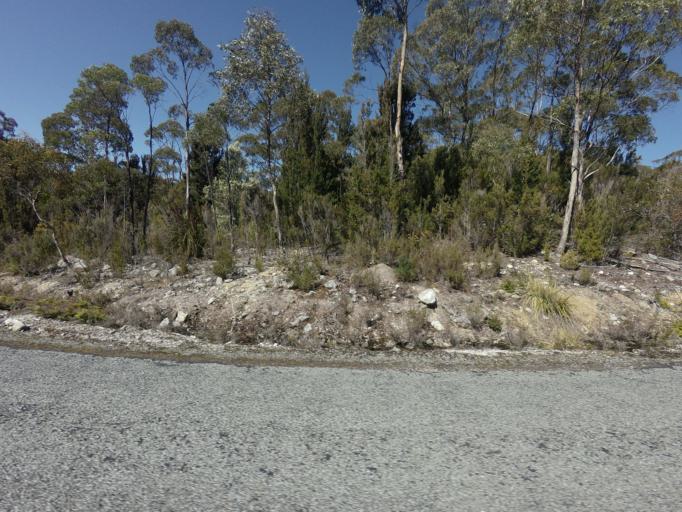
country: AU
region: Tasmania
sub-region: Huon Valley
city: Geeveston
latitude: -42.7701
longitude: 146.3967
